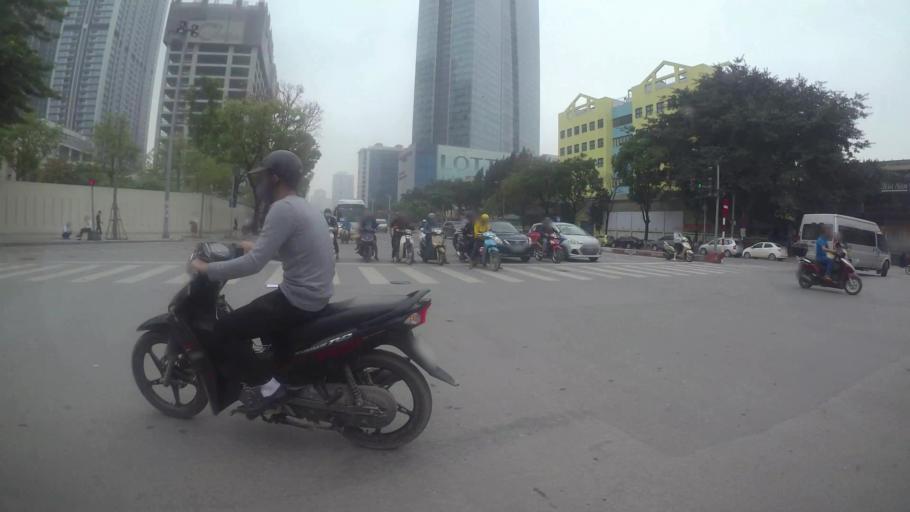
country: VN
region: Ha Noi
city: Cau Giay
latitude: 21.0339
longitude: 105.8141
